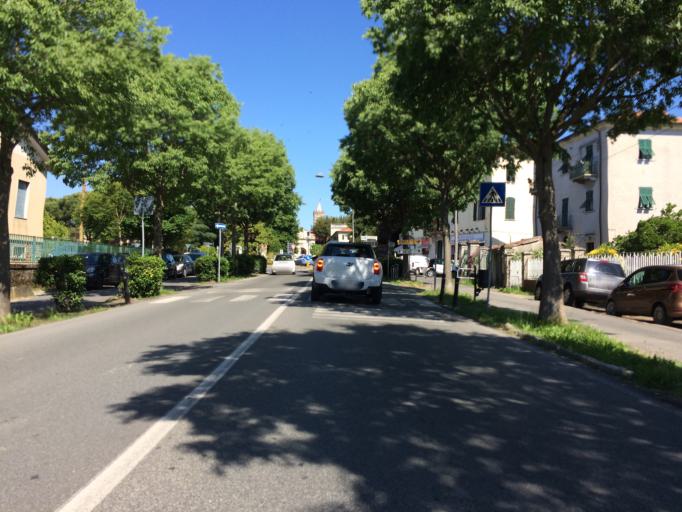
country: IT
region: Liguria
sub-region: Provincia di La Spezia
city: Sarzana
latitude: 44.1096
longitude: 9.9661
